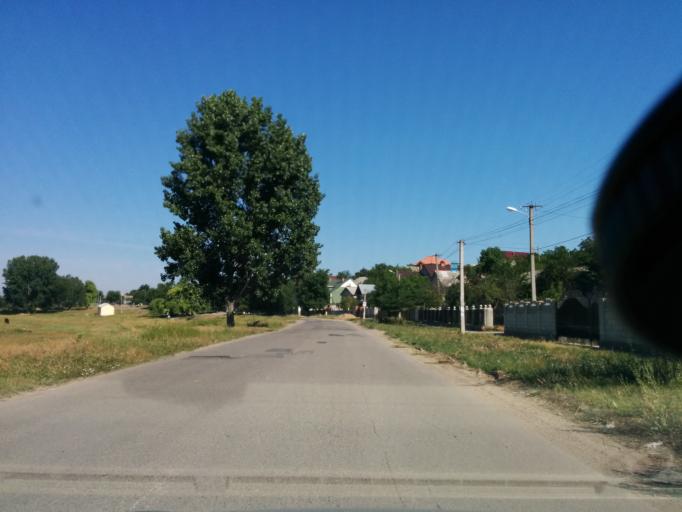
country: MD
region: Chisinau
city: Vadul lui Voda
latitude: 47.0637
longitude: 28.9963
